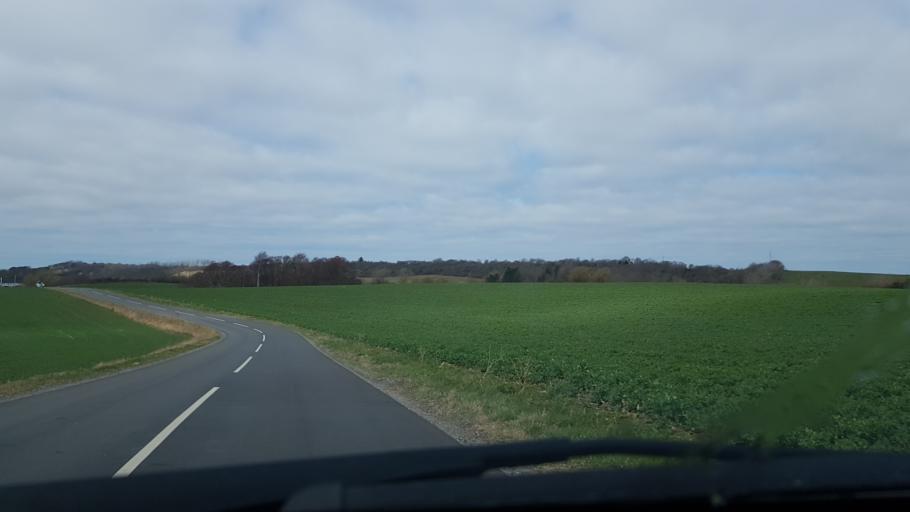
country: DK
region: Zealand
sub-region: Odsherred Kommune
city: Hojby
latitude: 55.9286
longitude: 11.5503
